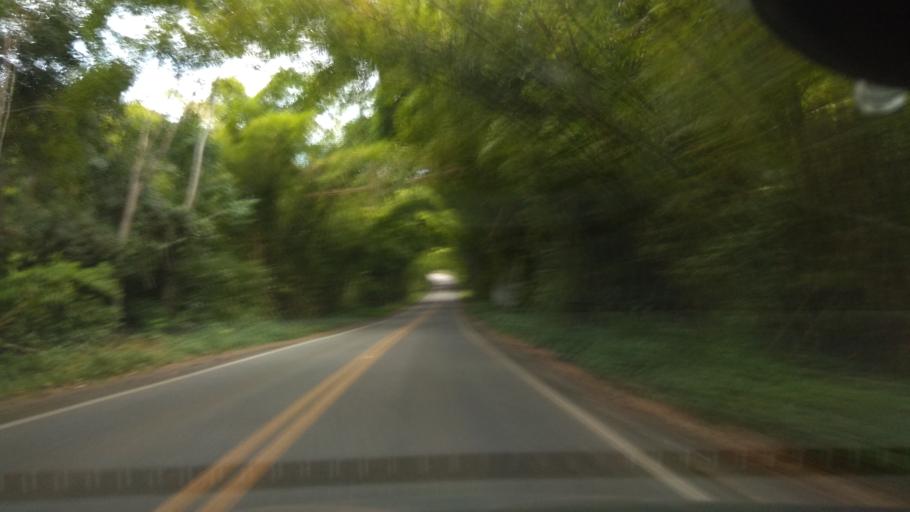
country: BR
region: Bahia
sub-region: Ibirapitanga
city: Ibirapitanga
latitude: -14.2350
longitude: -39.3851
